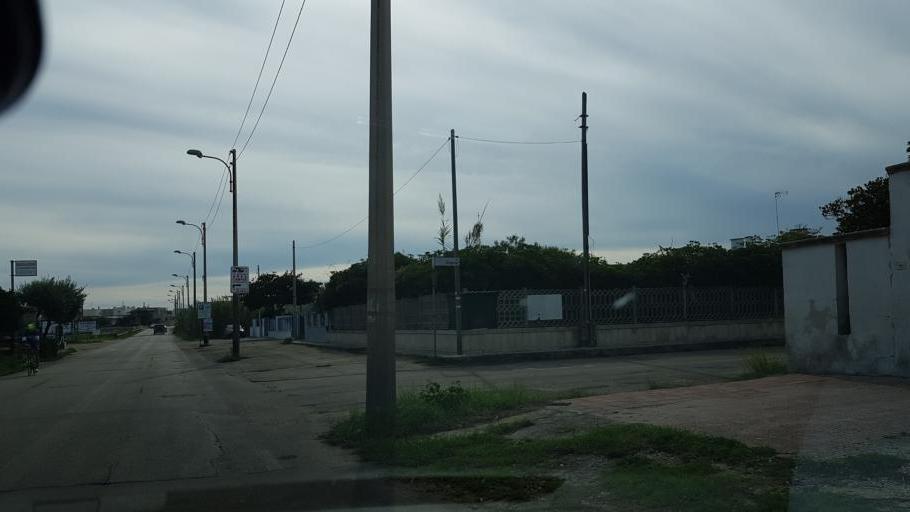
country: IT
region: Apulia
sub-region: Provincia di Lecce
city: Borgagne
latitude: 40.2945
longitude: 18.4181
